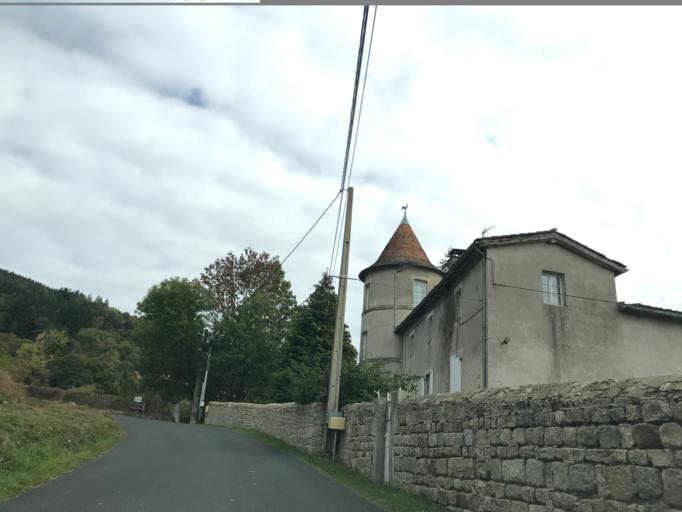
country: FR
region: Auvergne
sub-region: Departement du Puy-de-Dome
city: Celles-sur-Durolle
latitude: 45.8223
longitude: 3.6290
